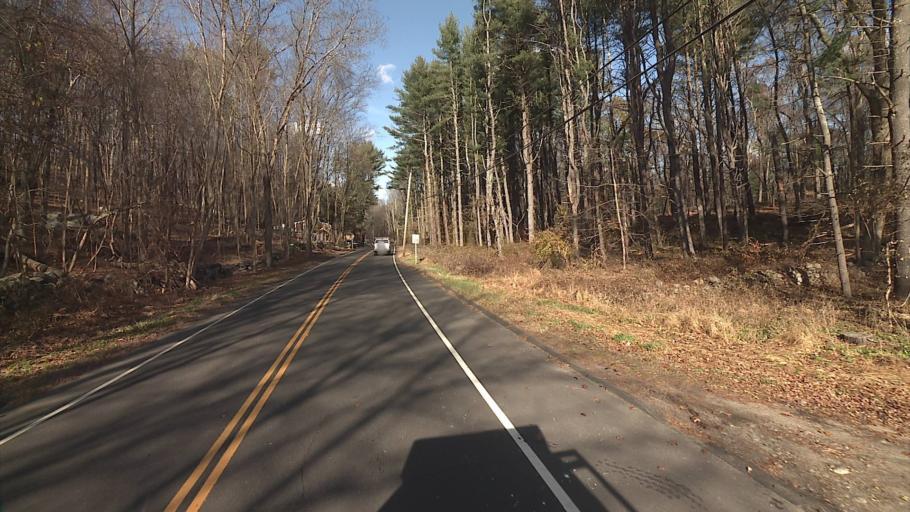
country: US
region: Connecticut
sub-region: Fairfield County
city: Georgetown
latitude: 41.2596
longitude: -73.3743
